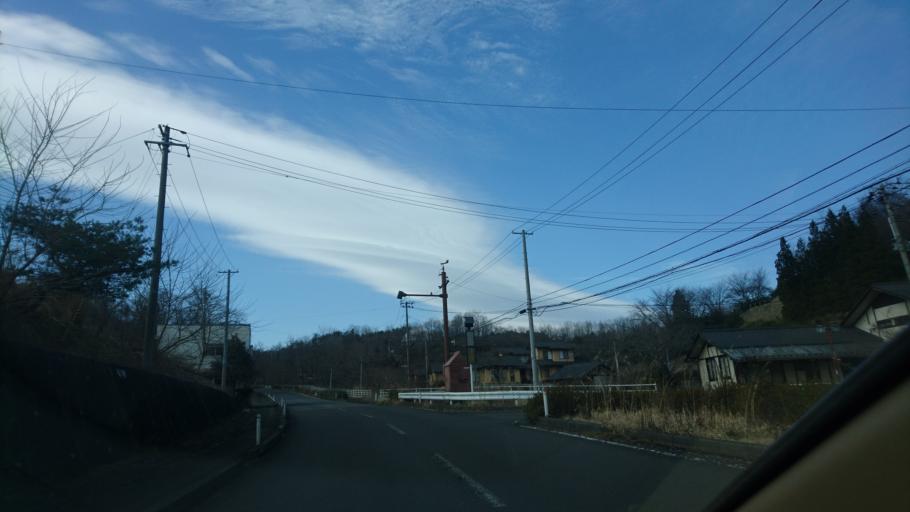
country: JP
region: Miyagi
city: Furukawa
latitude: 38.8050
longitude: 140.9047
